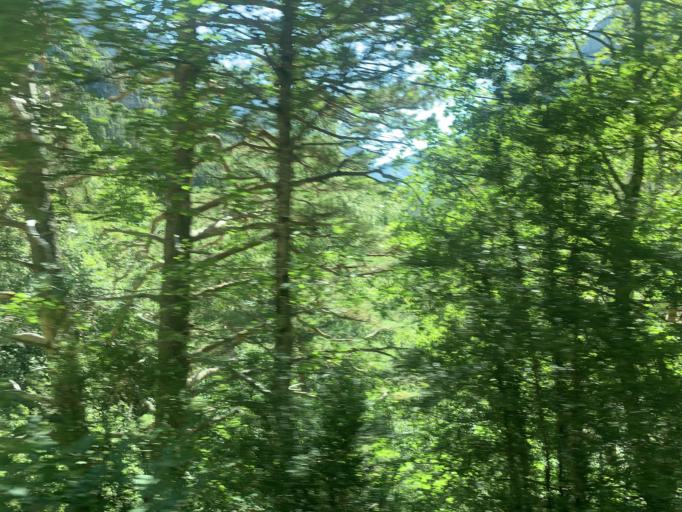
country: ES
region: Aragon
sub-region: Provincia de Huesca
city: Broto
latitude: 42.6556
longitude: -0.0850
